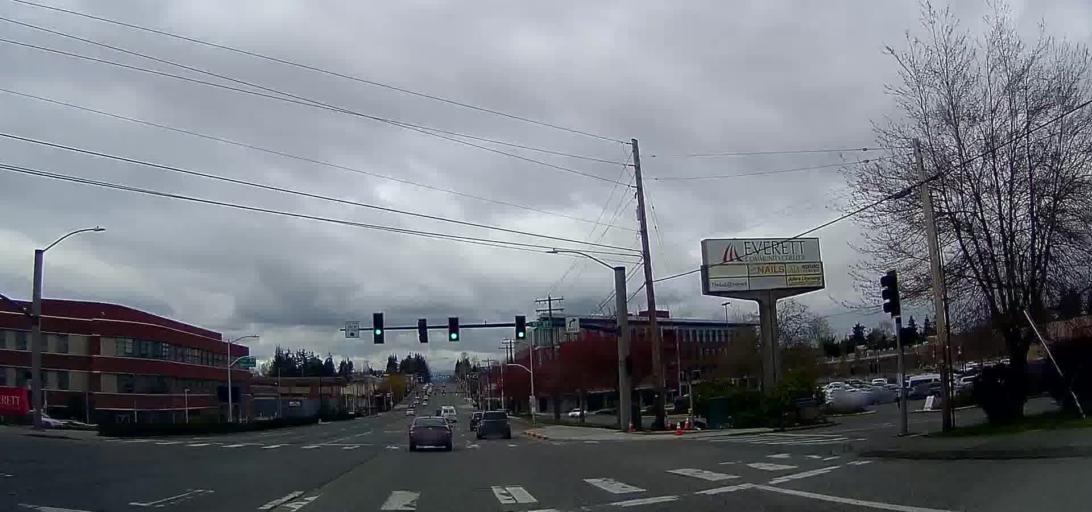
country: US
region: Washington
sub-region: Snohomish County
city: Everett
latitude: 48.0041
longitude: -122.1995
